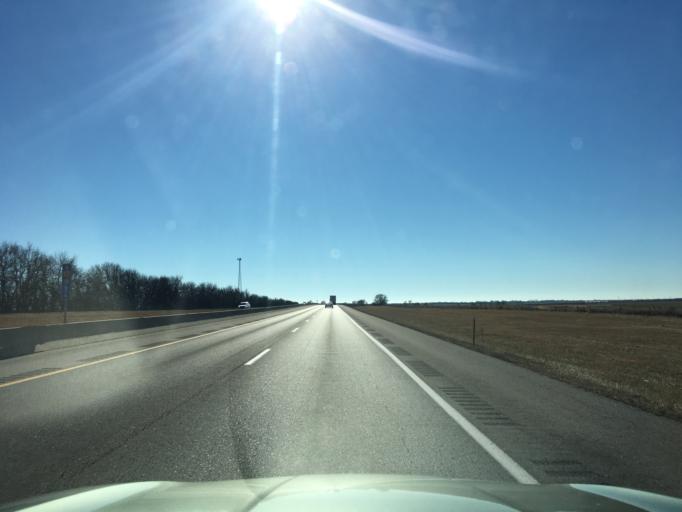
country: US
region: Kansas
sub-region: Sumner County
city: Wellington
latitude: 37.1235
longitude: -97.3389
